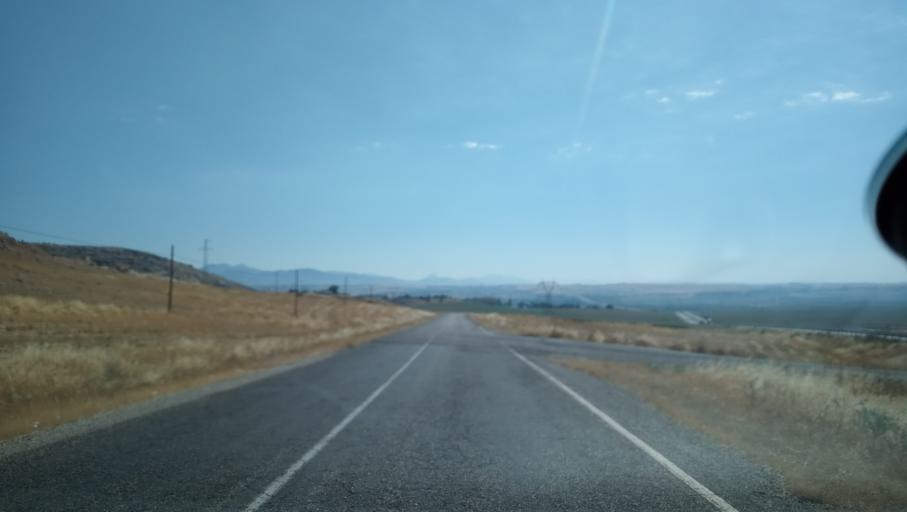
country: TR
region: Diyarbakir
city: Malabadi
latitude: 38.1285
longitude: 41.1750
